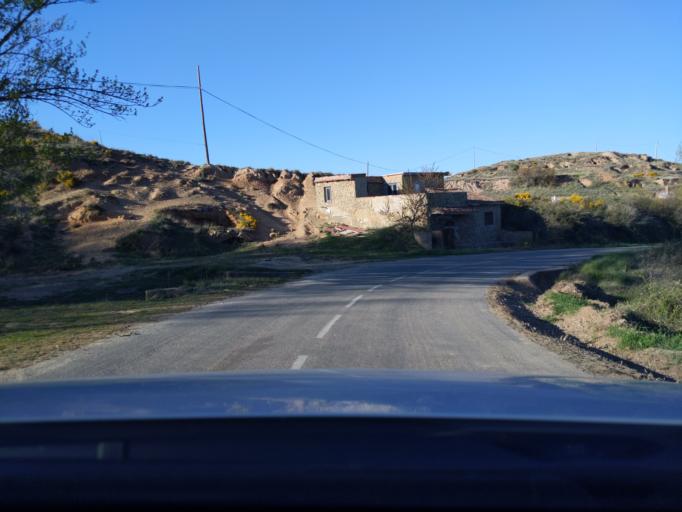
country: ES
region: La Rioja
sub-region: Provincia de La Rioja
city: Bergasa
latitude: 42.2497
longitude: -2.1354
